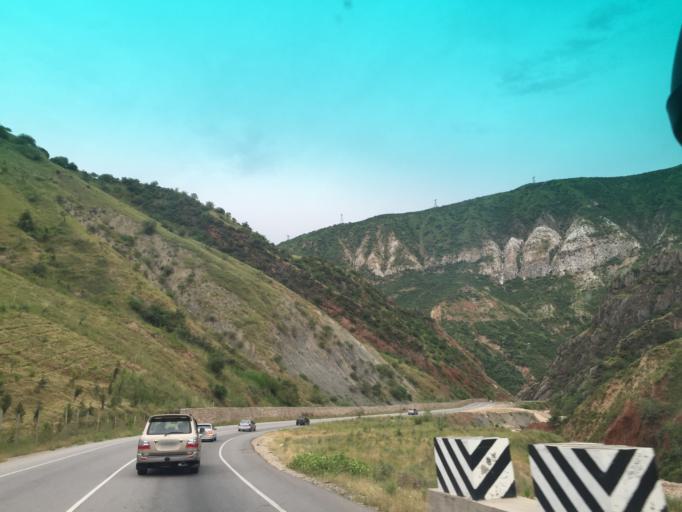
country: TJ
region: Khatlon
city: Norak
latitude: 38.4349
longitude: 69.2082
